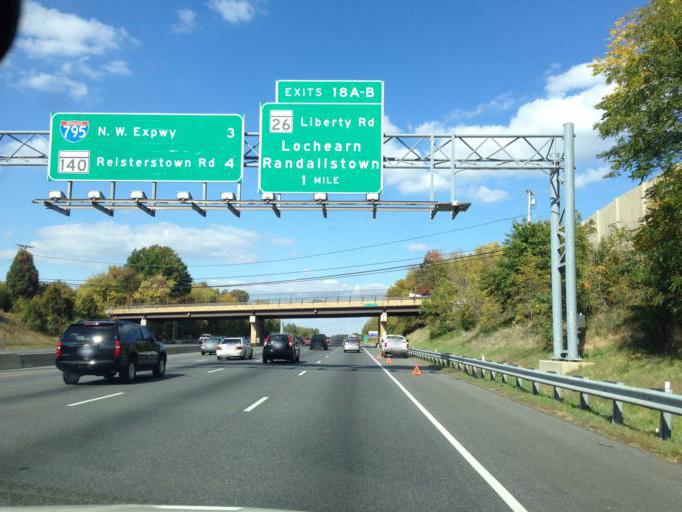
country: US
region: Maryland
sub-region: Baltimore County
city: Woodlawn
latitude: 39.3320
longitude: -76.7445
